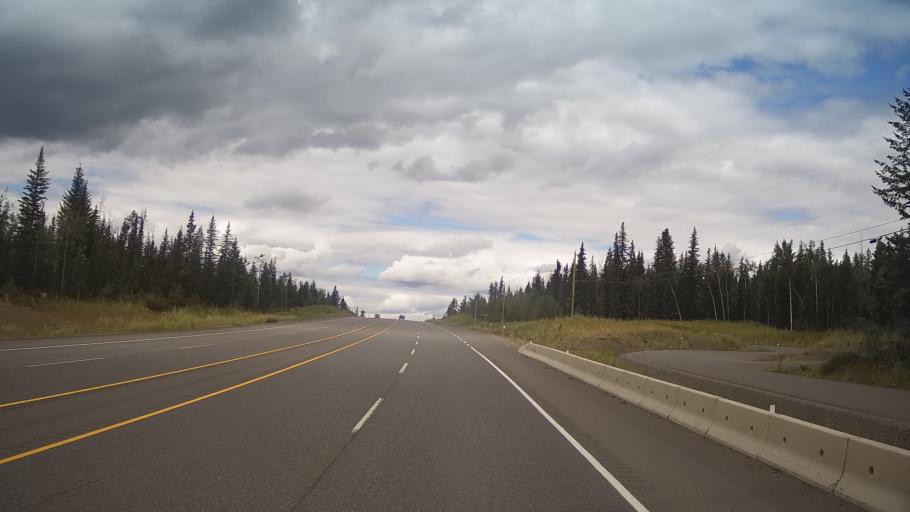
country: CA
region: British Columbia
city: Cache Creek
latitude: 51.3884
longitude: -121.3664
